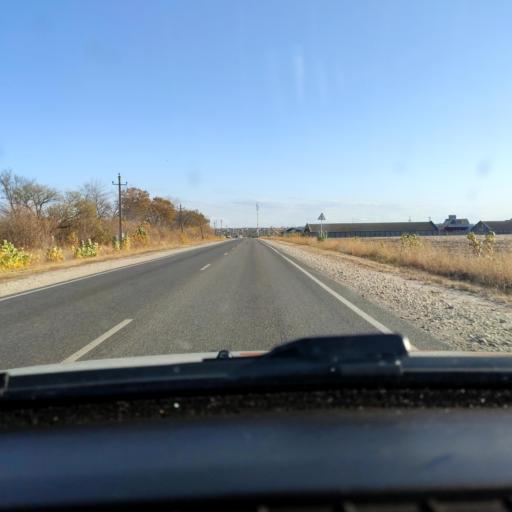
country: RU
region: Voronezj
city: Semiluki
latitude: 51.7254
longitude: 38.9904
